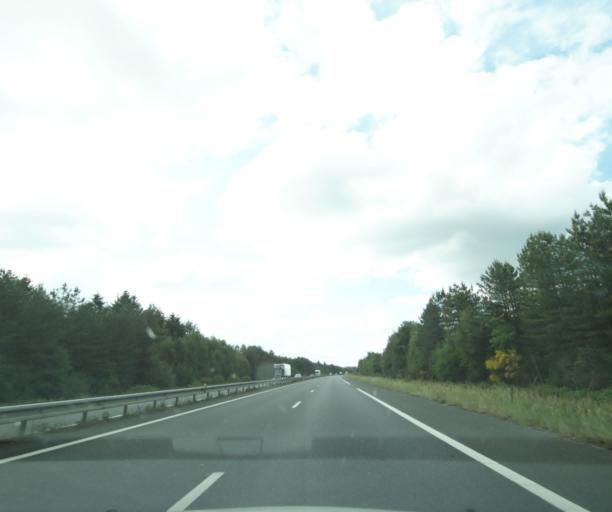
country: FR
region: Centre
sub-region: Departement du Loir-et-Cher
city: Lamotte-Beuvron
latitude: 47.6011
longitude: 1.9763
